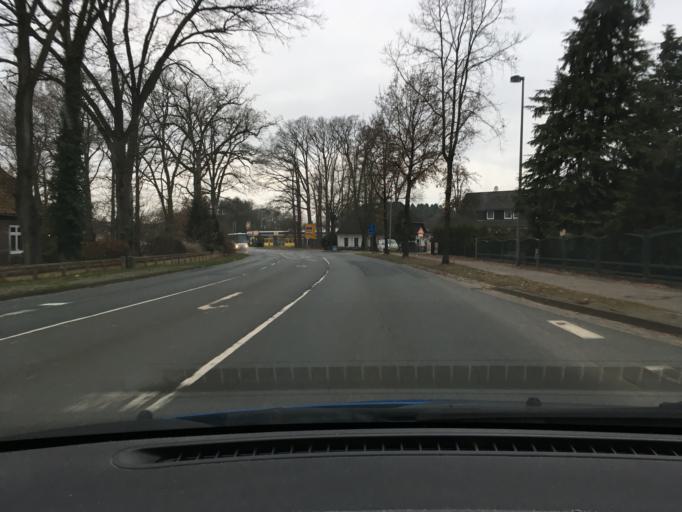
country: DE
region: Lower Saxony
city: Walsrode
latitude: 52.8677
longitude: 9.6299
